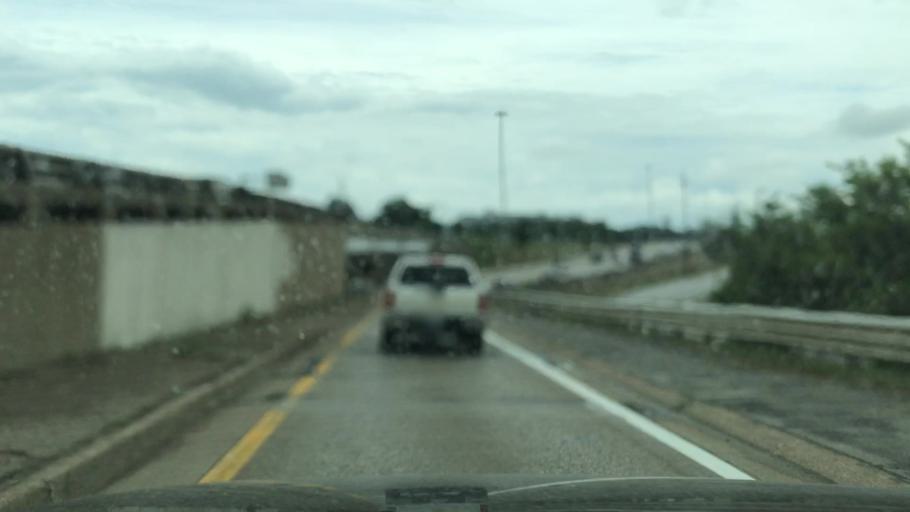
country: US
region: Michigan
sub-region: Kent County
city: Grand Rapids
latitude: 42.9741
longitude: -85.6772
